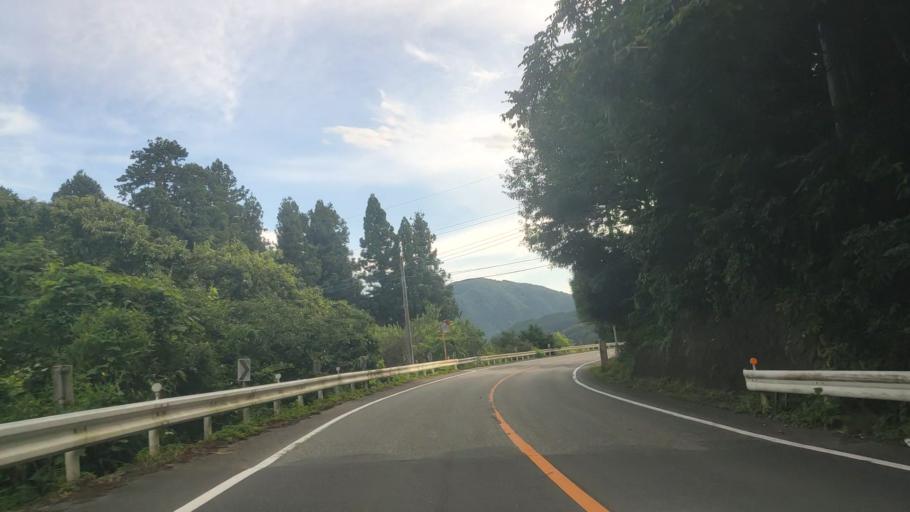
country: JP
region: Gunma
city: Omamacho-omama
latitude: 36.5169
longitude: 139.3027
